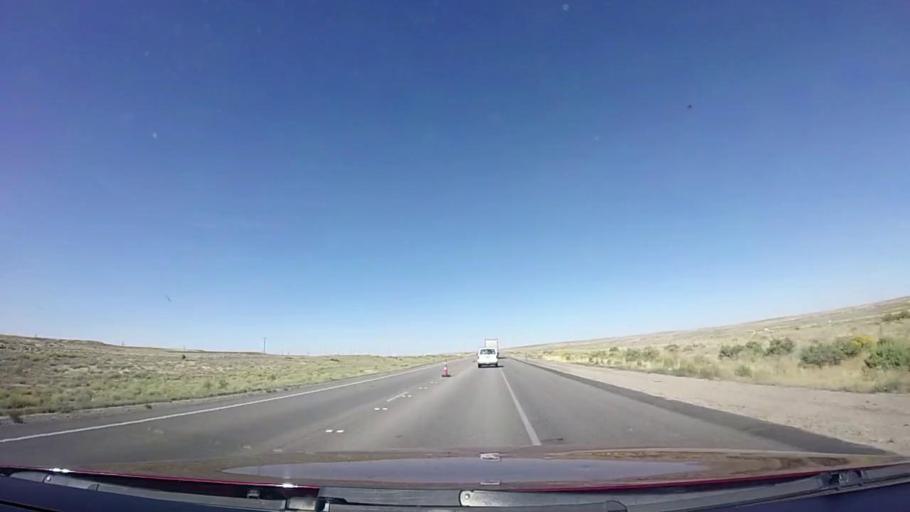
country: US
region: Wyoming
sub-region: Carbon County
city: Rawlins
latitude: 41.7056
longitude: -107.8849
